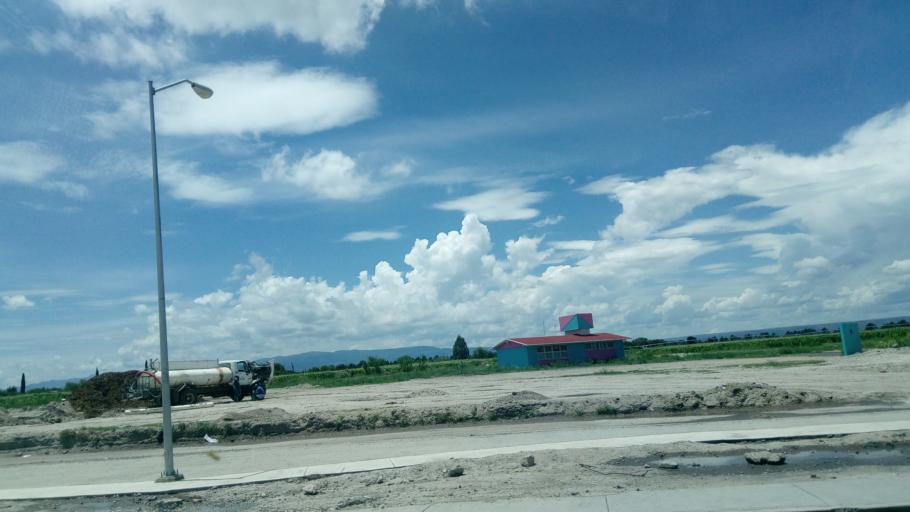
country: MX
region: Durango
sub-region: Durango
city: Jose Refugio Salcido
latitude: 24.0144
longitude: -104.5437
